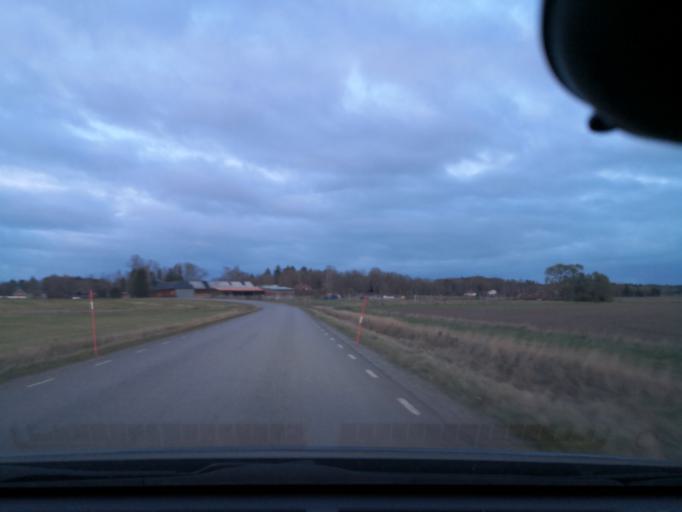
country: SE
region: Uppsala
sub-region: Enkopings Kommun
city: Irsta
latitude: 59.6997
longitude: 16.9959
